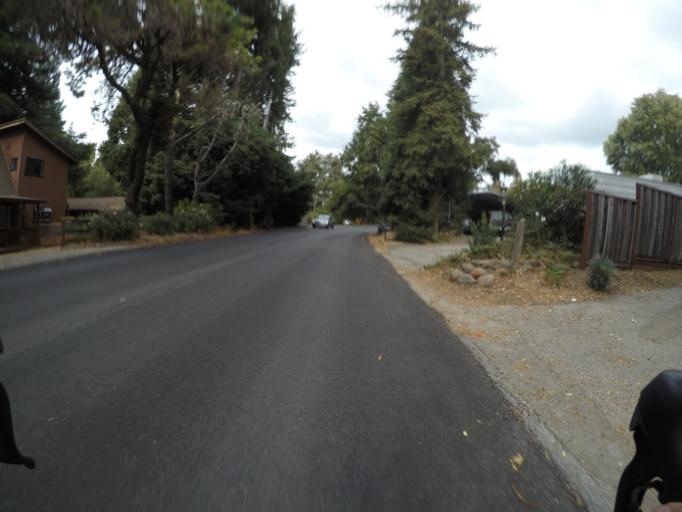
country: US
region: California
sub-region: Santa Cruz County
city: Ben Lomond
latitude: 37.0773
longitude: -122.0803
